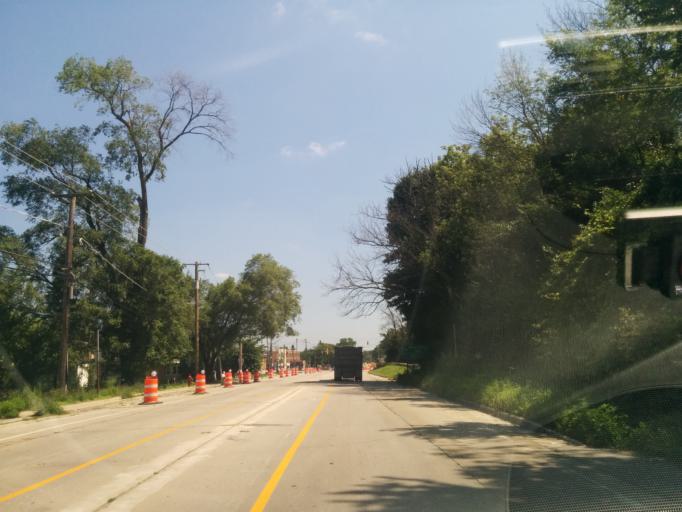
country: US
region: Illinois
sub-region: Cook County
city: Willow Springs
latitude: 41.7307
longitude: -87.8790
